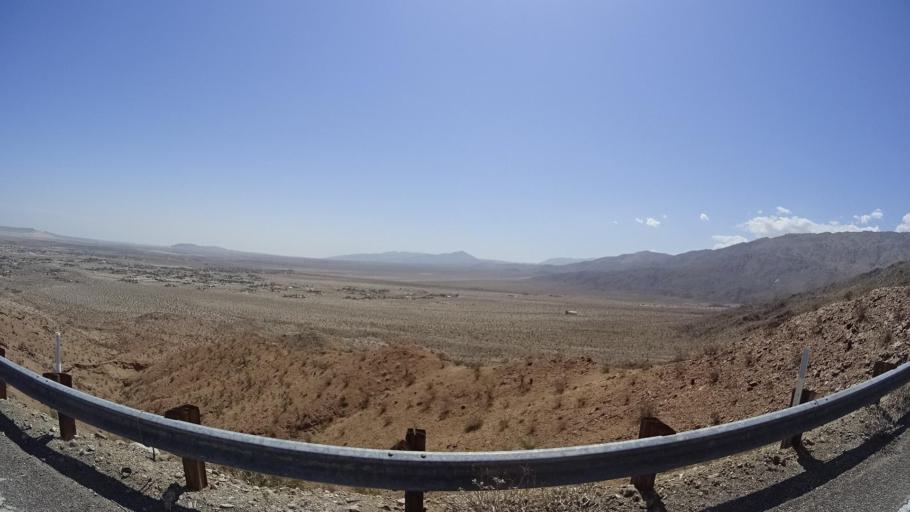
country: US
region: California
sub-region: San Diego County
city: Borrego Springs
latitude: 33.2369
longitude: -116.4063
